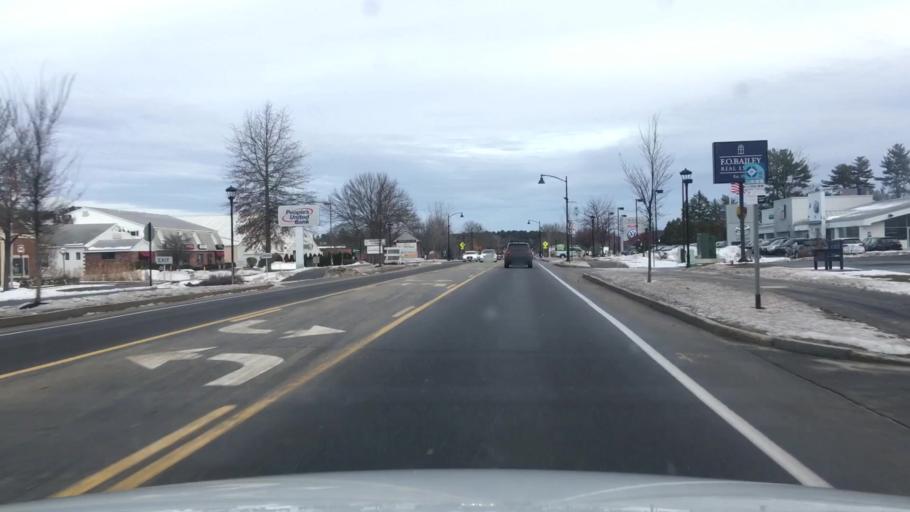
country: US
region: Maine
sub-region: Cumberland County
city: Falmouth
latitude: 43.7153
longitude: -70.2335
